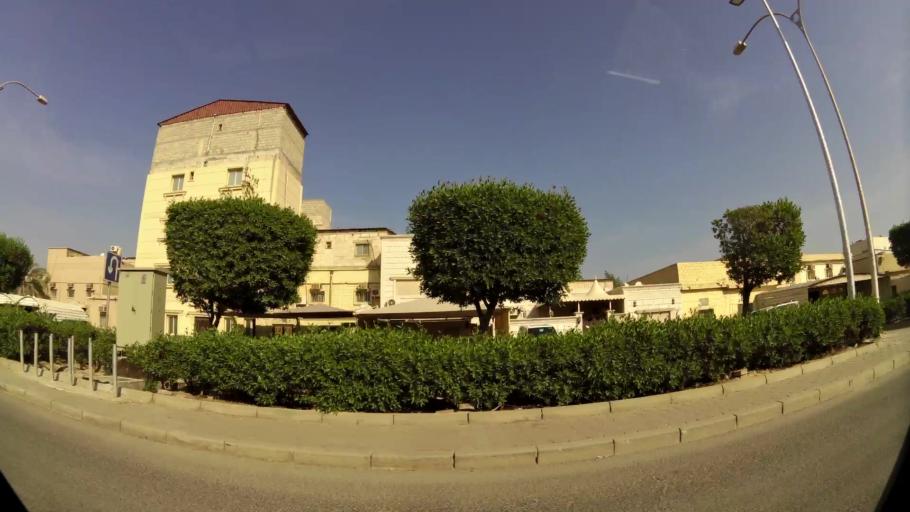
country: KW
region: Al Ahmadi
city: Ar Riqqah
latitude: 29.1376
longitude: 48.1086
